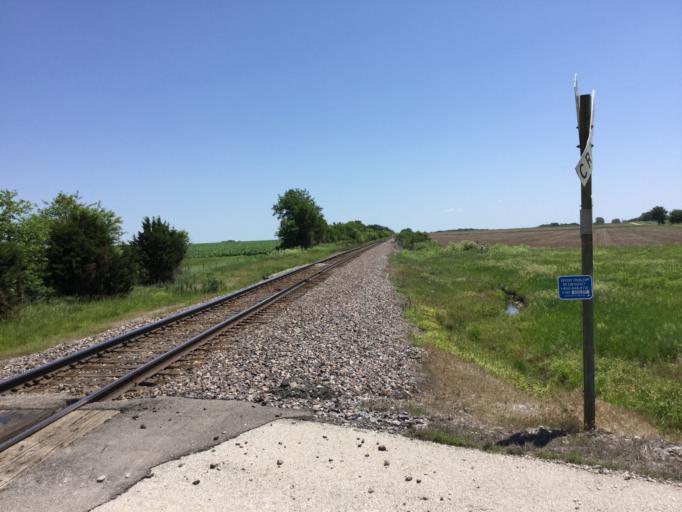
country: US
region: Kansas
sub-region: Anderson County
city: Garnett
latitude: 38.1545
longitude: -95.0951
